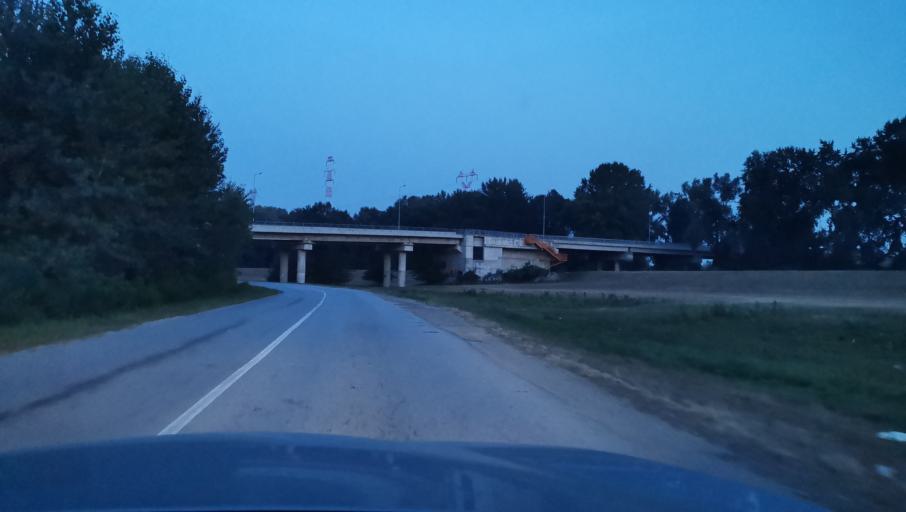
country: RS
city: Zvecka
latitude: 44.6777
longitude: 20.1678
